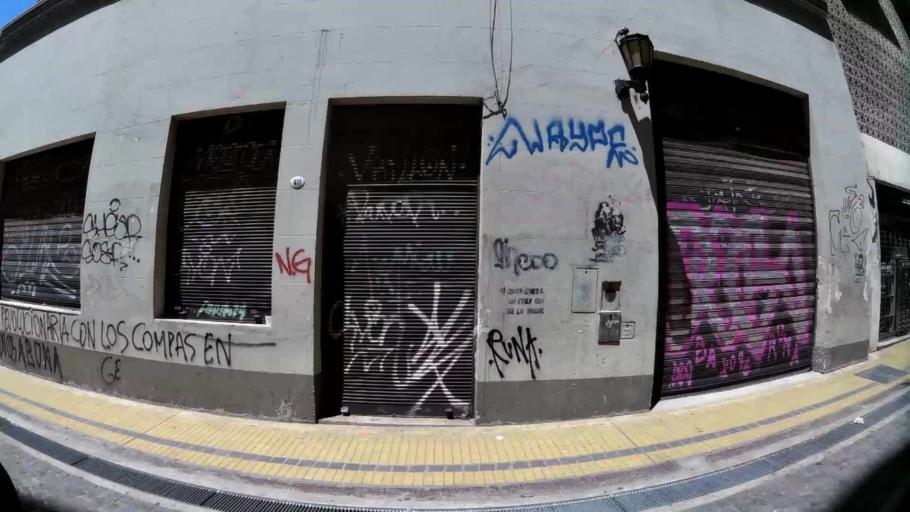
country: AR
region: Buenos Aires F.D.
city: Buenos Aires
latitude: -34.6114
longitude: -58.3724
